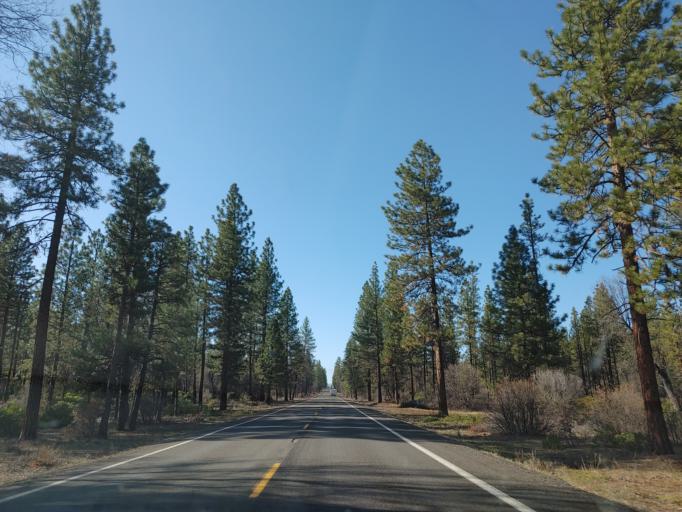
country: US
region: California
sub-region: Shasta County
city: Burney
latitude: 40.9245
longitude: -121.5984
